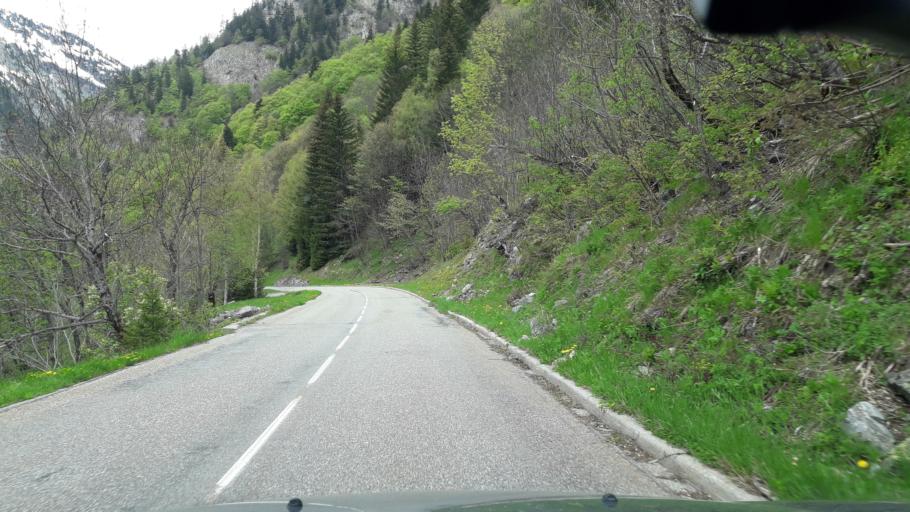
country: FR
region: Rhone-Alpes
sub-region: Departement de l'Isere
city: Huez
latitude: 45.2045
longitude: 6.0954
